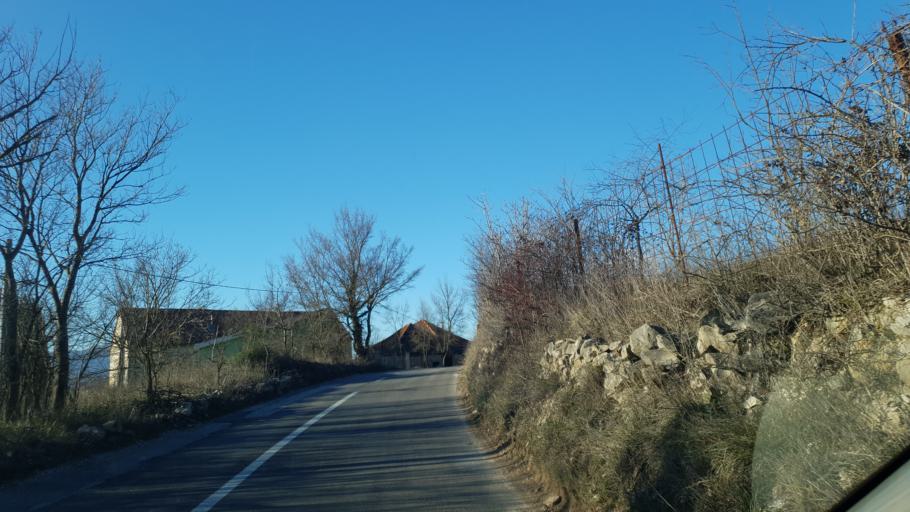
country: HR
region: Splitsko-Dalmatinska
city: Gala
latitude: 43.7340
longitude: 16.6865
